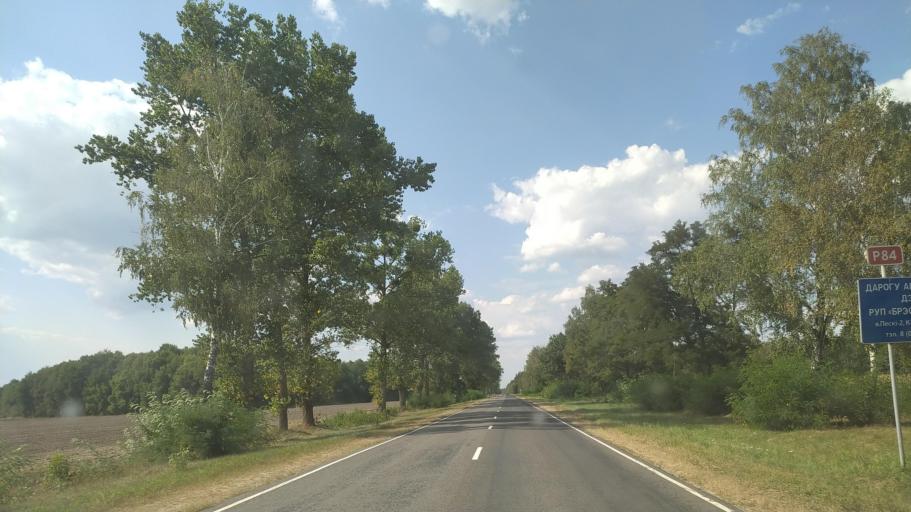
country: BY
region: Brest
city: Drahichyn
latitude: 52.2086
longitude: 25.1397
